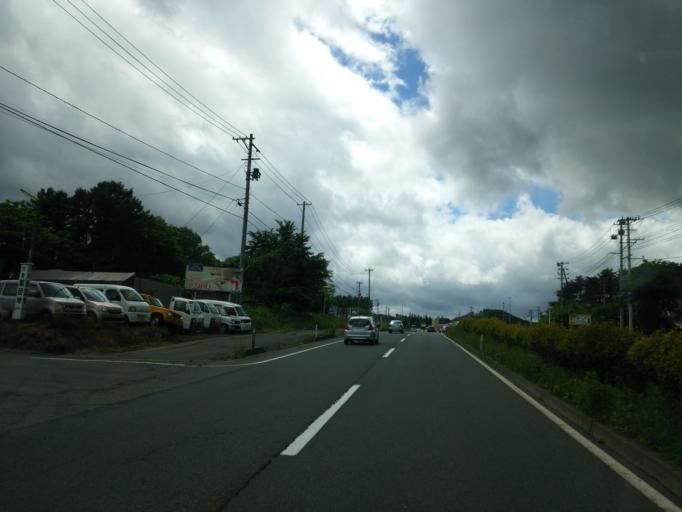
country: JP
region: Iwate
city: Shizukuishi
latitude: 39.7020
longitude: 141.0377
